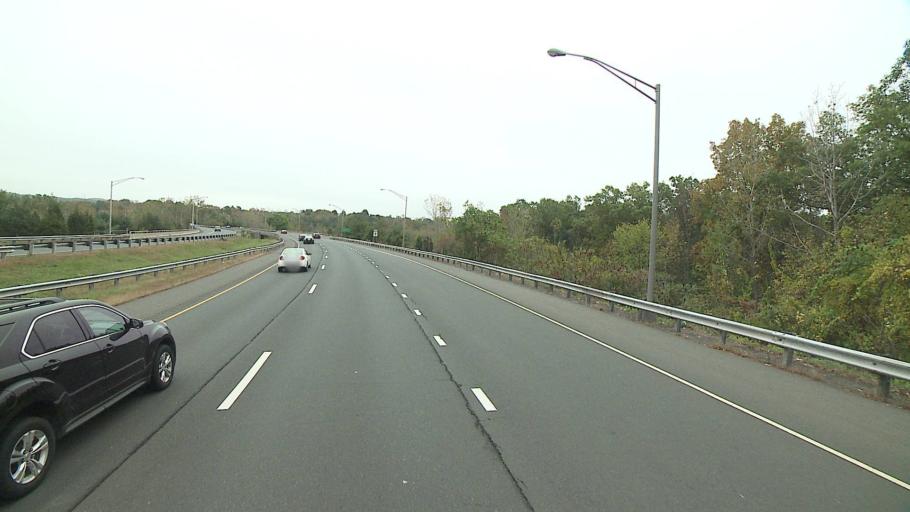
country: US
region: Connecticut
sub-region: Hartford County
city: Kensington
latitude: 41.6214
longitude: -72.7348
